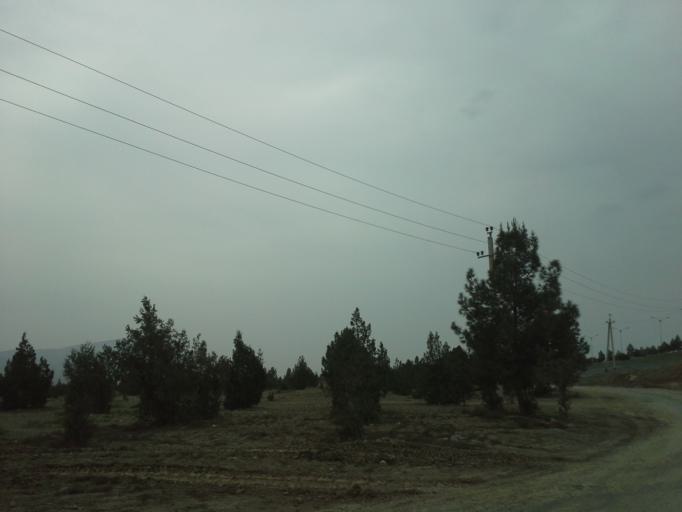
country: TM
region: Ahal
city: Abadan
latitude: 37.9828
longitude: 58.2259
